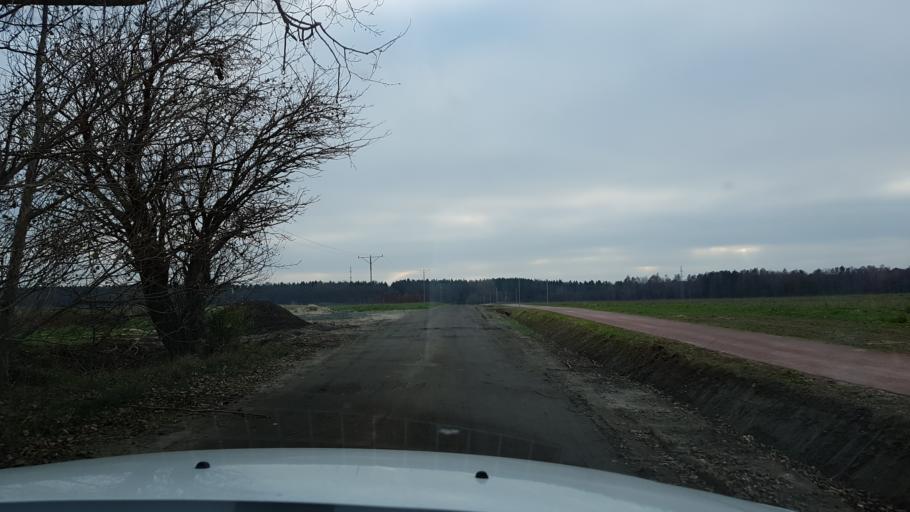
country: PL
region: West Pomeranian Voivodeship
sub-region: Powiat kolobrzeski
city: Grzybowo
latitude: 54.1405
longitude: 15.5150
